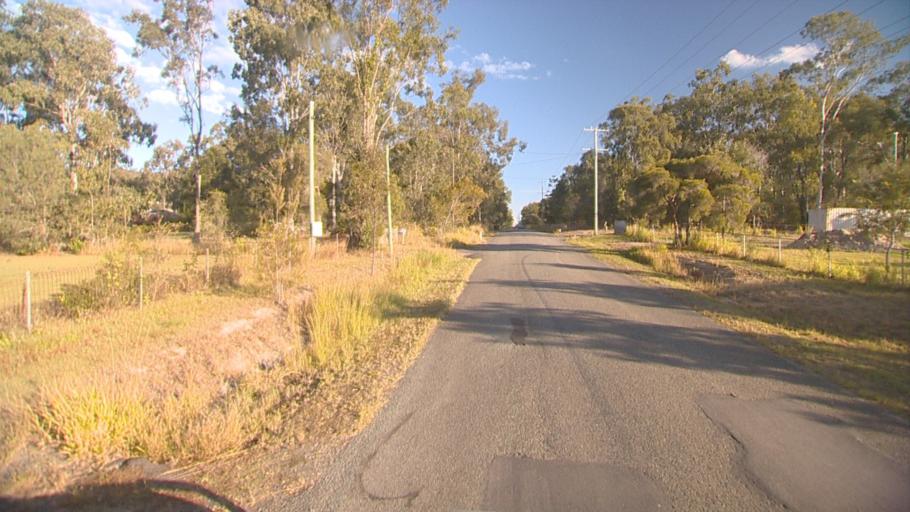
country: AU
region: Queensland
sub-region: Logan
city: Waterford West
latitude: -27.7255
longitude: 153.1531
